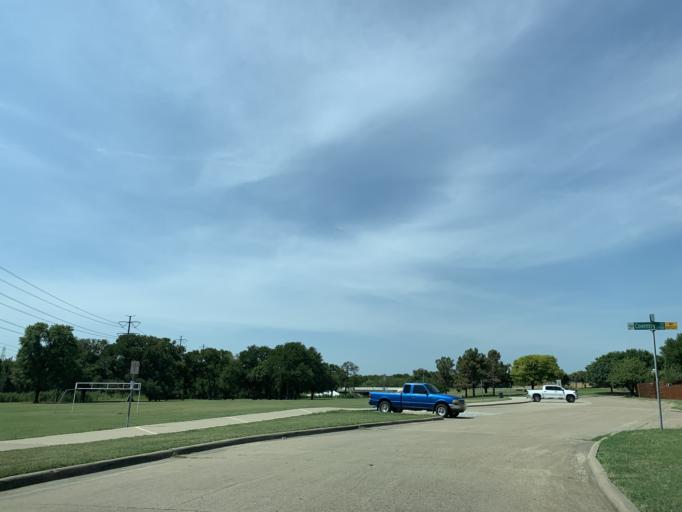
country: US
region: Texas
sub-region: Dallas County
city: Grand Prairie
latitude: 32.6614
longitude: -97.0401
